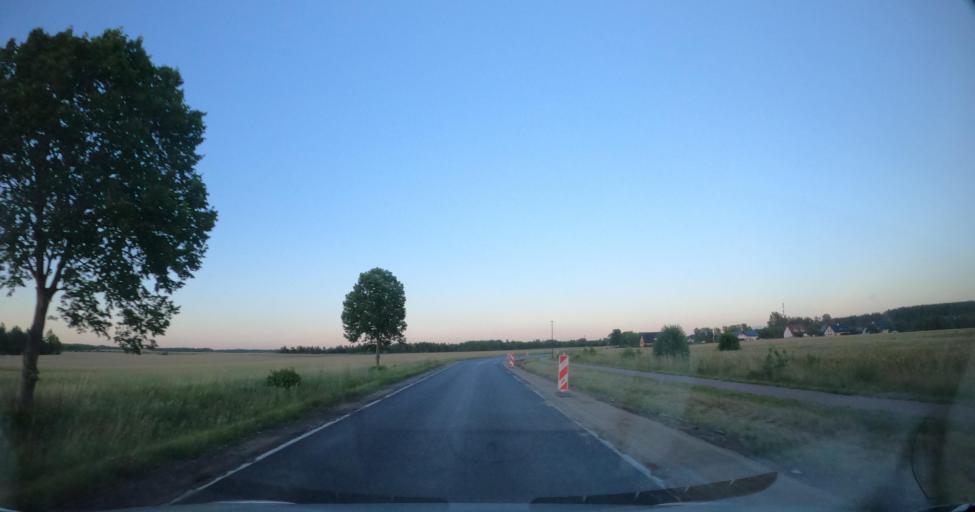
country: PL
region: Pomeranian Voivodeship
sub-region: Powiat wejherowski
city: Linia
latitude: 54.4546
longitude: 17.9145
